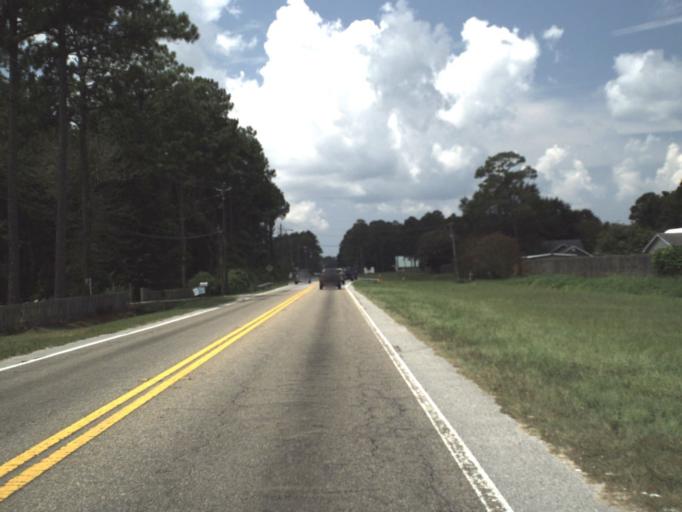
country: US
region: Florida
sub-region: Bay County
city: Hiland Park
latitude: 30.2333
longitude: -85.6163
